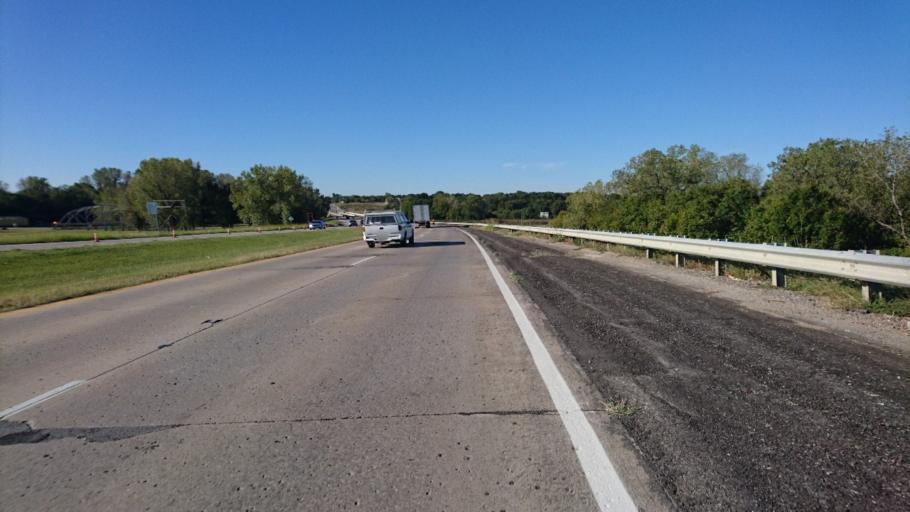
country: US
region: Oklahoma
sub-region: Rogers County
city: Catoosa
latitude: 36.2142
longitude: -95.7220
